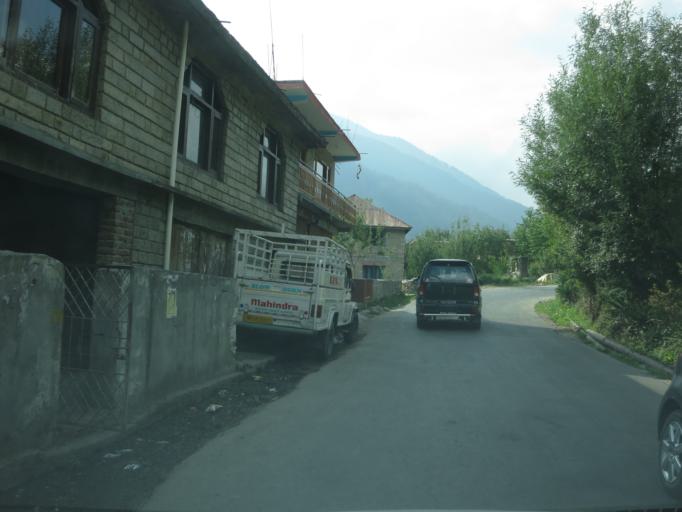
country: IN
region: Himachal Pradesh
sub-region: Kulu
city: Nagar
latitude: 32.1666
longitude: 77.1920
